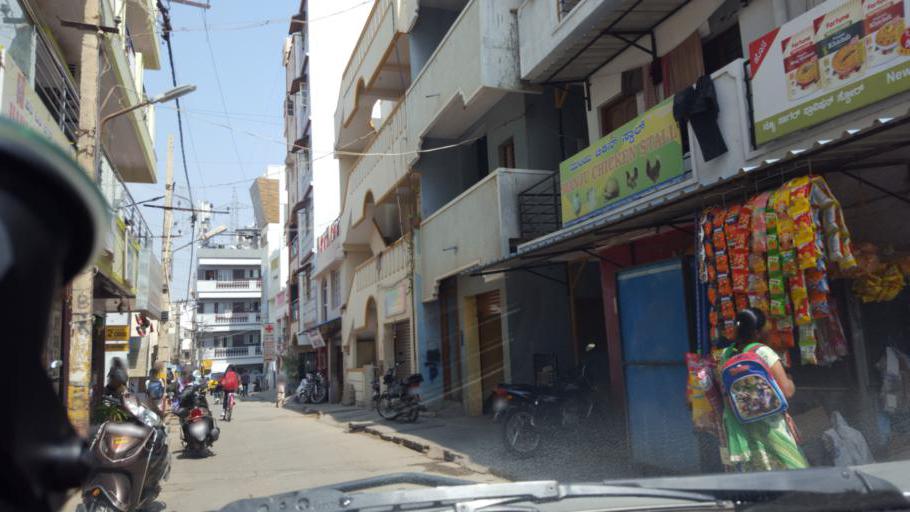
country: IN
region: Karnataka
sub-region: Bangalore Urban
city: Bangalore
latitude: 12.9756
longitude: 77.6704
